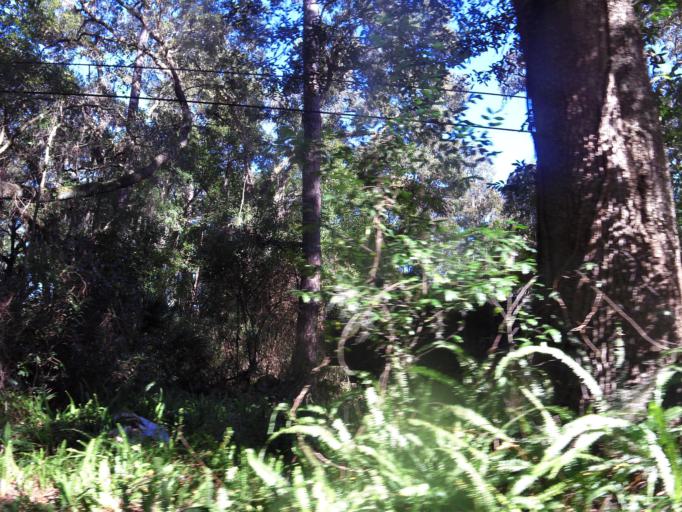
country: US
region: Florida
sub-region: Duval County
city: Jacksonville
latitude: 30.2796
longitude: -81.6483
